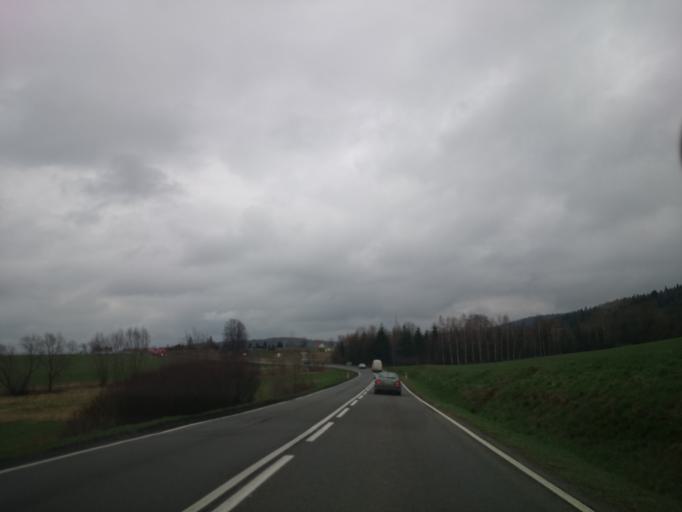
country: PL
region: Lower Silesian Voivodeship
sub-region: Powiat zabkowicki
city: Zloty Stok
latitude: 50.4479
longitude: 16.8598
